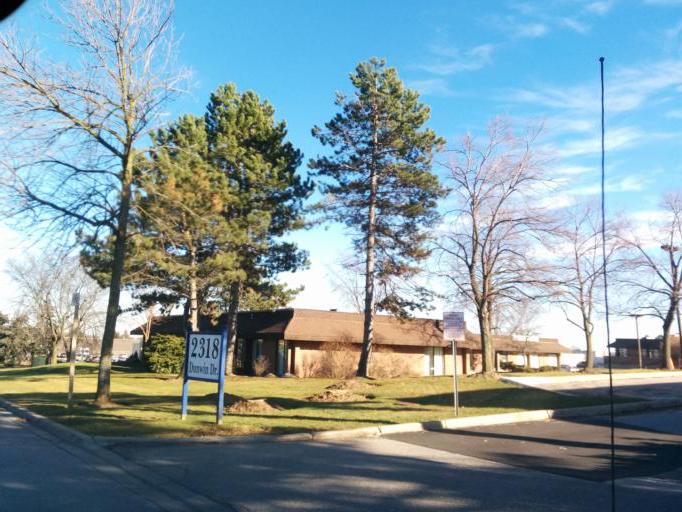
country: CA
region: Ontario
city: Mississauga
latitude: 43.5336
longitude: -79.6767
